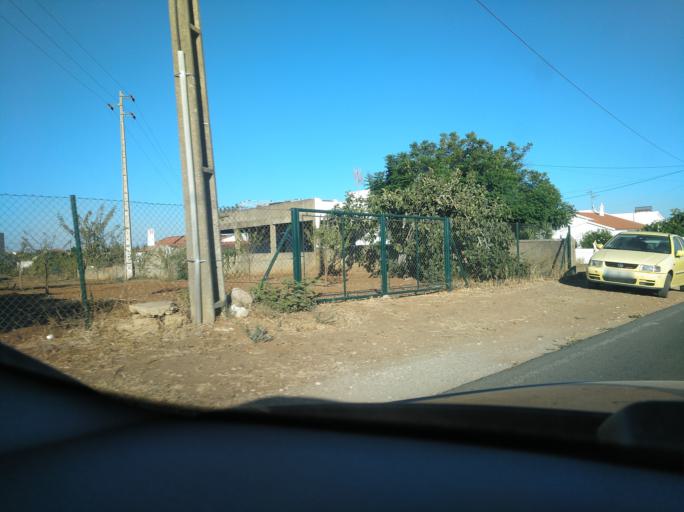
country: PT
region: Faro
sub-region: Vila Real de Santo Antonio
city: Monte Gordo
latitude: 37.1810
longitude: -7.5184
